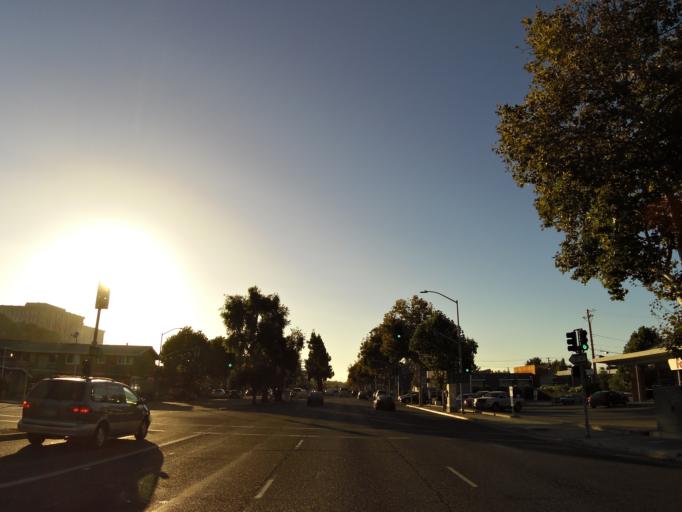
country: US
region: California
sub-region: Santa Clara County
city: Palo Alto
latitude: 37.4208
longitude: -122.1377
